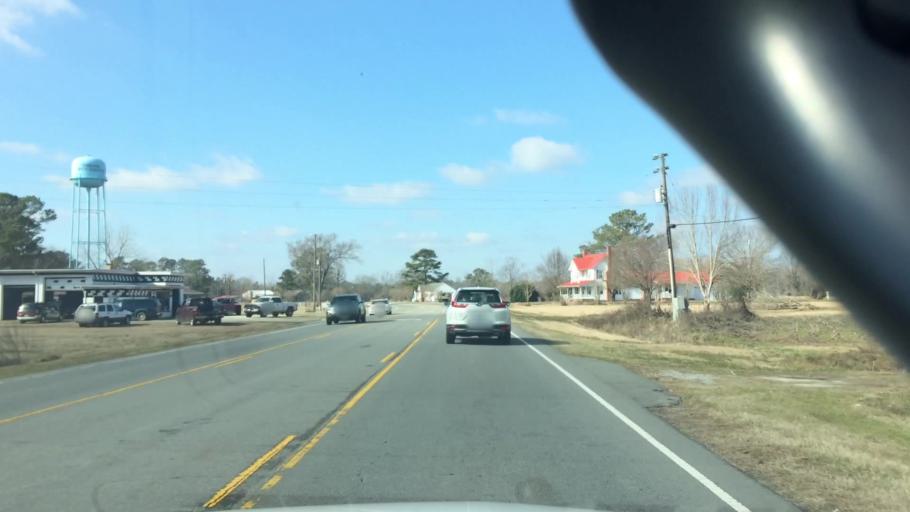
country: US
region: North Carolina
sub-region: Duplin County
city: Beulaville
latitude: 34.8326
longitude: -77.8214
